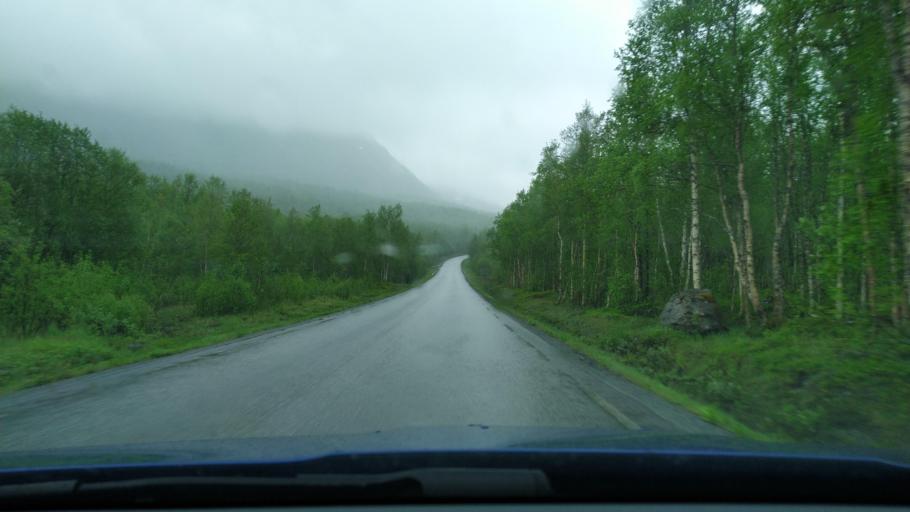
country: NO
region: Troms
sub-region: Dyroy
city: Brostadbotn
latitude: 69.0212
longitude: 17.7371
